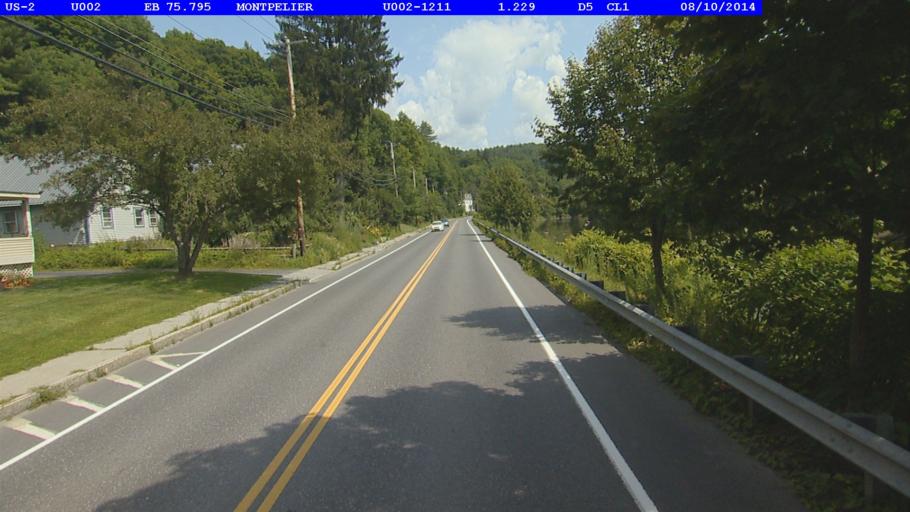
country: US
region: Vermont
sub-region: Washington County
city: Montpelier
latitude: 44.2603
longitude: -72.5913
